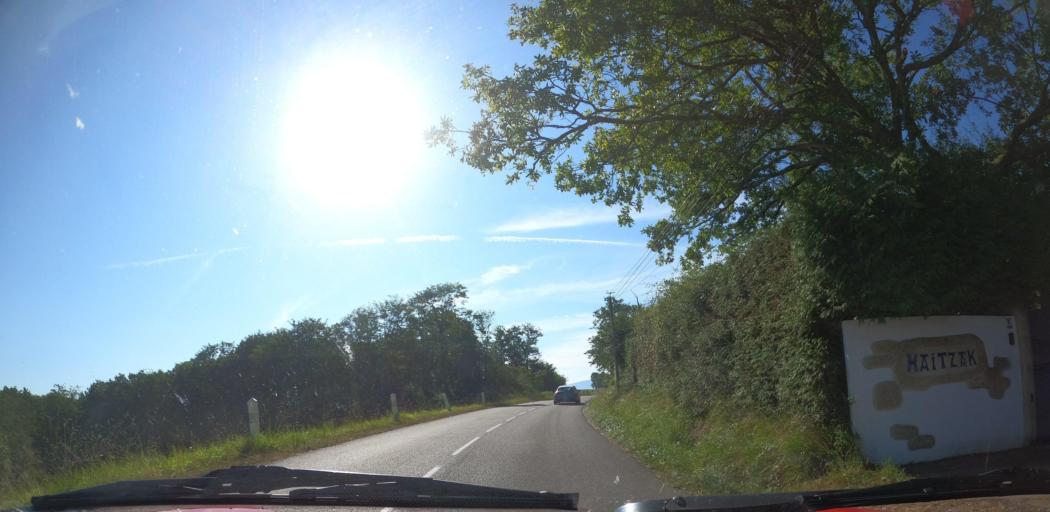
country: FR
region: Aquitaine
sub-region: Departement des Pyrenees-Atlantiques
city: Arcangues
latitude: 43.4008
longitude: -1.5345
